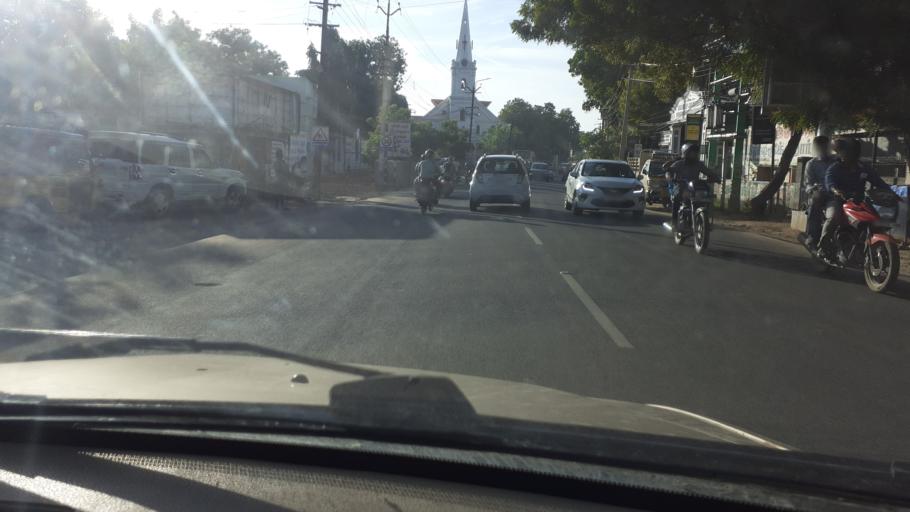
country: IN
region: Tamil Nadu
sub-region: Tirunelveli Kattabo
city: Tirunelveli
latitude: 8.7264
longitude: 77.7288
